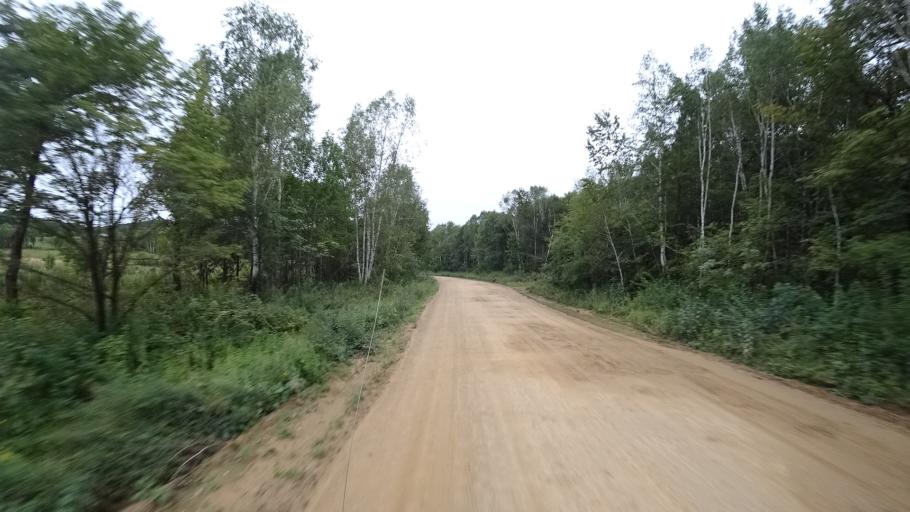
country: RU
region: Primorskiy
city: Rettikhovka
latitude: 44.1802
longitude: 132.8745
